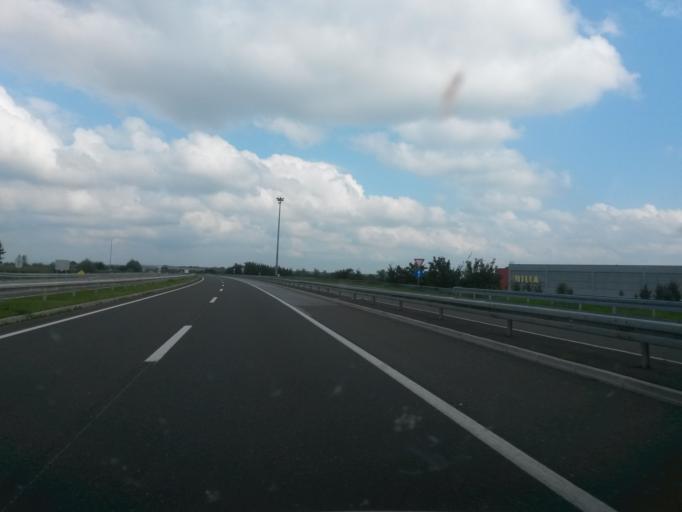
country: HR
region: Zagrebacka
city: Brckovljani
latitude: 45.9047
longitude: 16.2723
